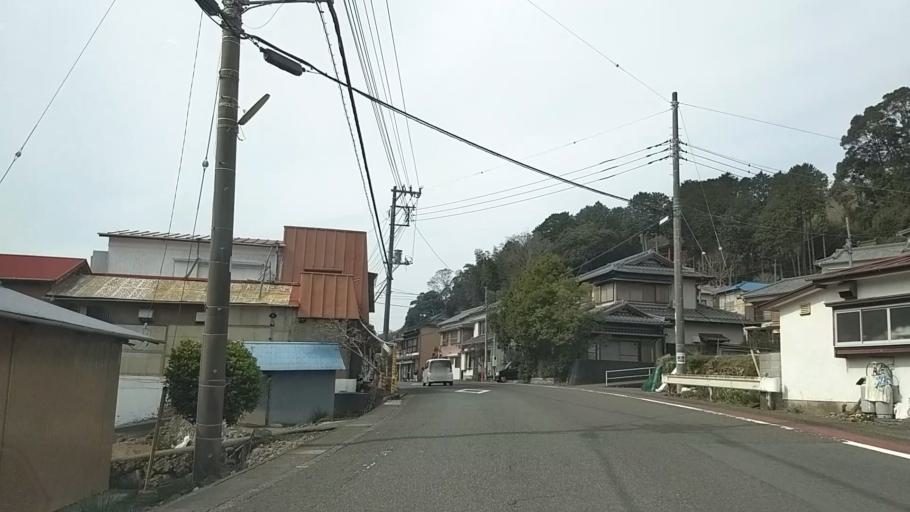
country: JP
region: Shizuoka
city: Shimoda
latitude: 34.7232
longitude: 138.9382
